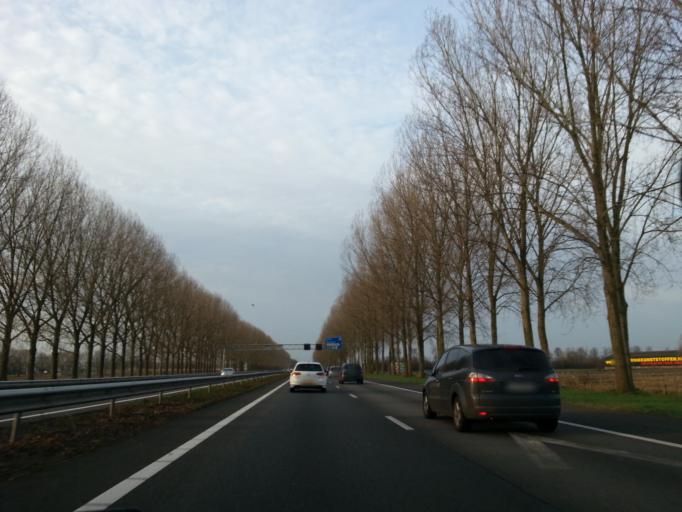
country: NL
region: Gelderland
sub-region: Gemeente Zevenaar
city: Zevenaar
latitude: 51.9311
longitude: 6.1056
